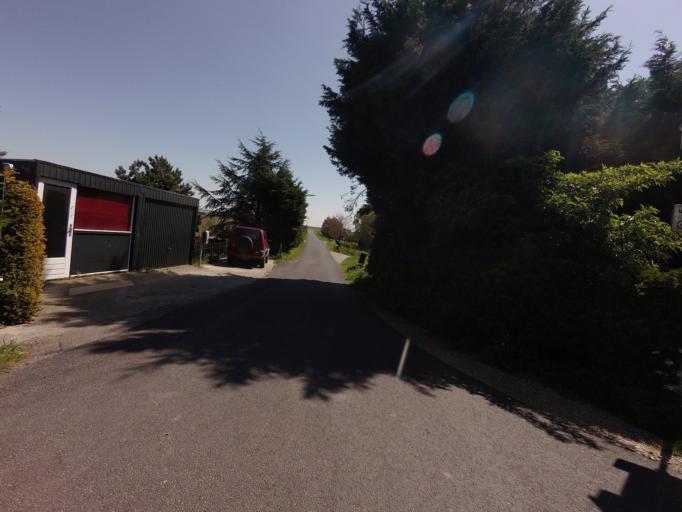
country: NL
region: South Holland
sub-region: Gemeente Dordrecht
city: Dordrecht
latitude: 51.7662
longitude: 4.6562
